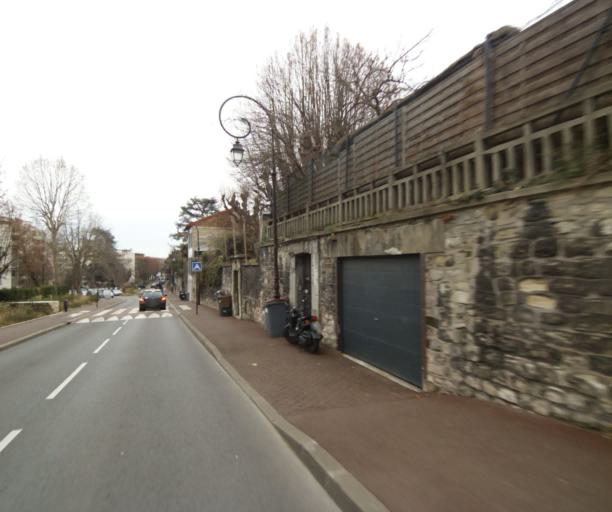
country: FR
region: Ile-de-France
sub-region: Departement des Hauts-de-Seine
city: Saint-Cloud
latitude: 48.8497
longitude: 2.2180
